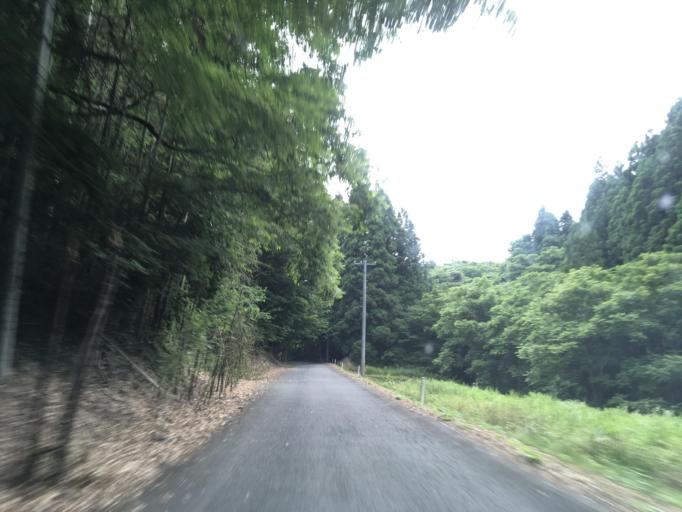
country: JP
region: Iwate
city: Ichinoseki
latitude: 38.8490
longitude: 141.3219
